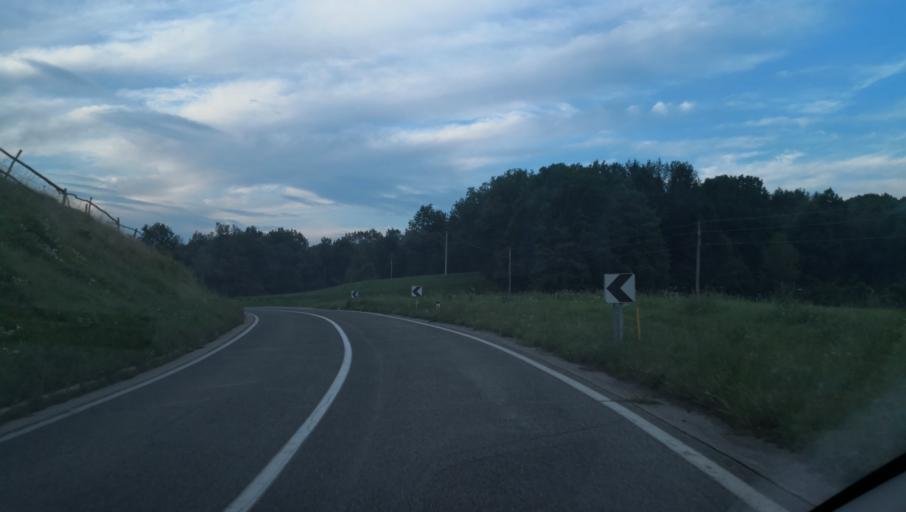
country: SI
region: Metlika
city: Metlika
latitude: 45.6620
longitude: 15.2893
